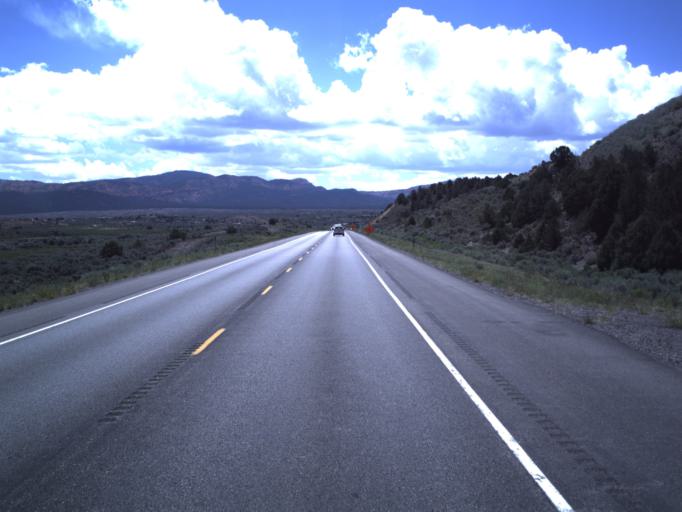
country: US
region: Utah
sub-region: Garfield County
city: Panguitch
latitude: 37.7667
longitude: -112.3884
